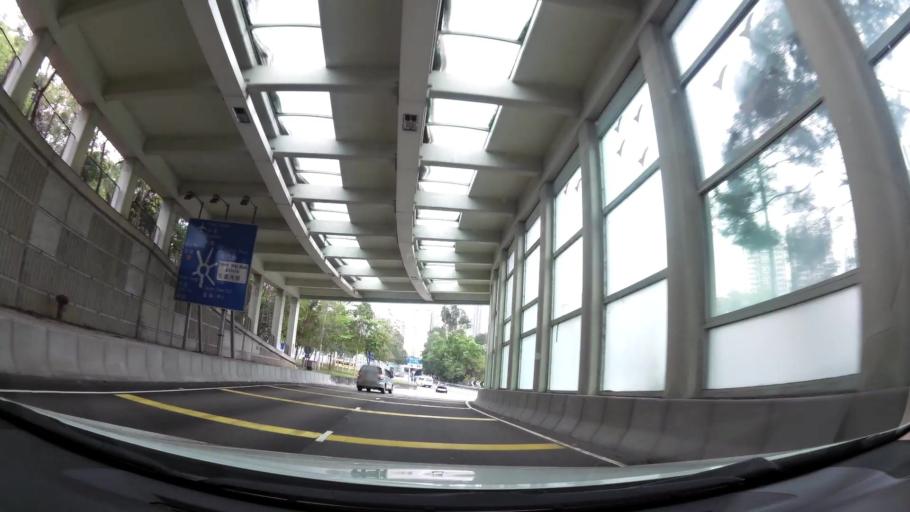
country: HK
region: Tsuen Wan
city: Tsuen Wan
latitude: 22.3757
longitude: 114.1193
